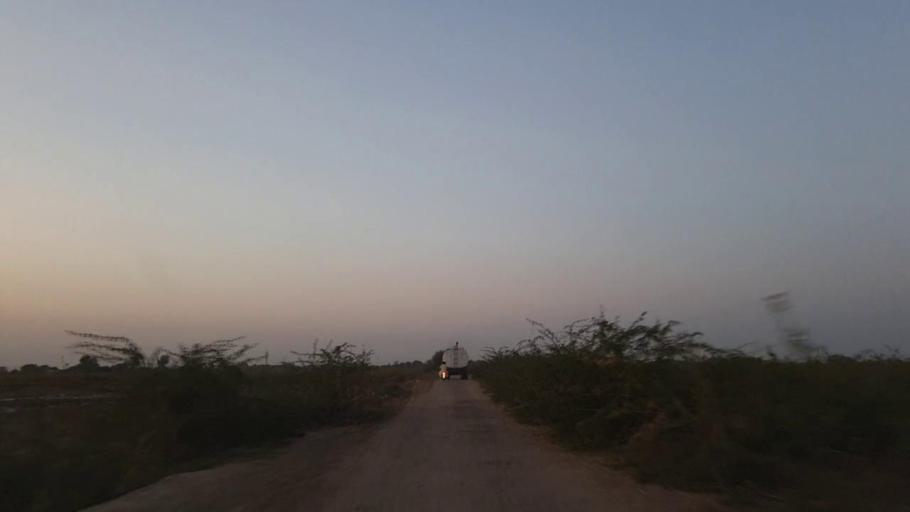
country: PK
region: Sindh
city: Naukot
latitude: 24.9004
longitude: 69.3804
